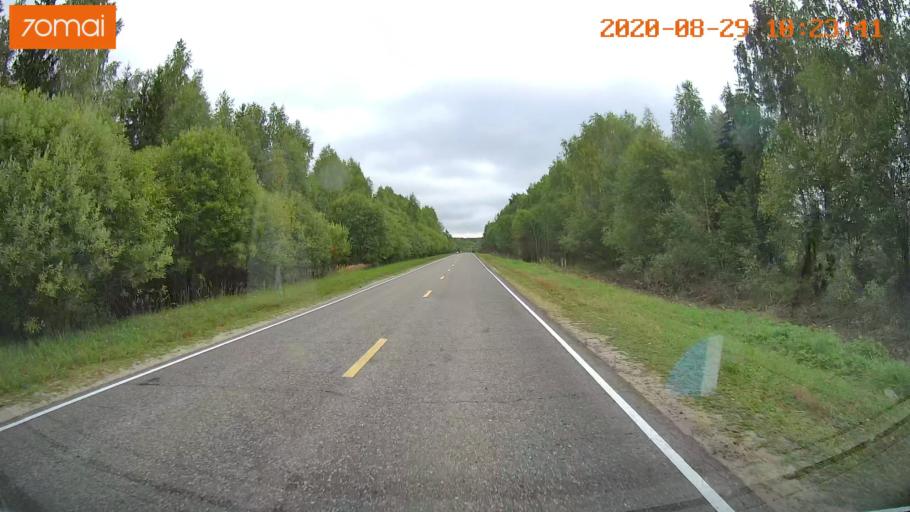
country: RU
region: Ivanovo
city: Yur'yevets
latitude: 57.3232
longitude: 42.9794
